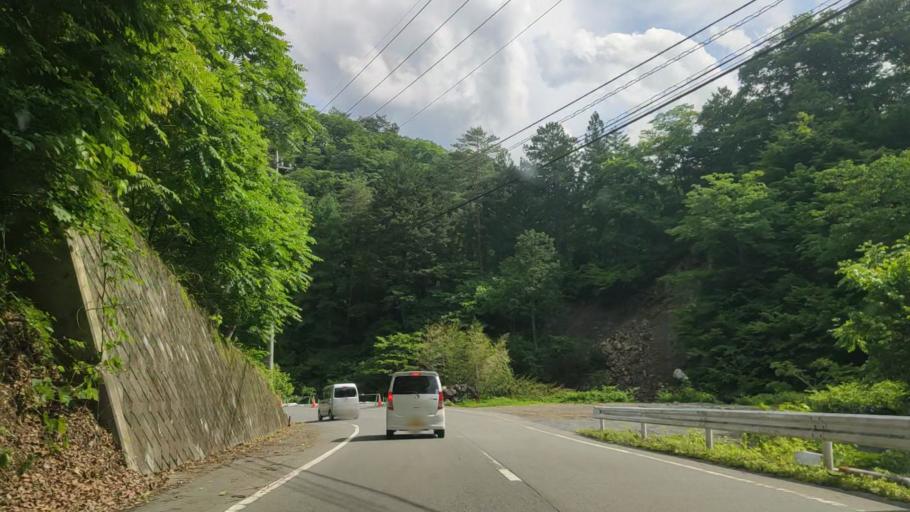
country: JP
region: Gunma
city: Tomioka
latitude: 36.0950
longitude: 138.7169
